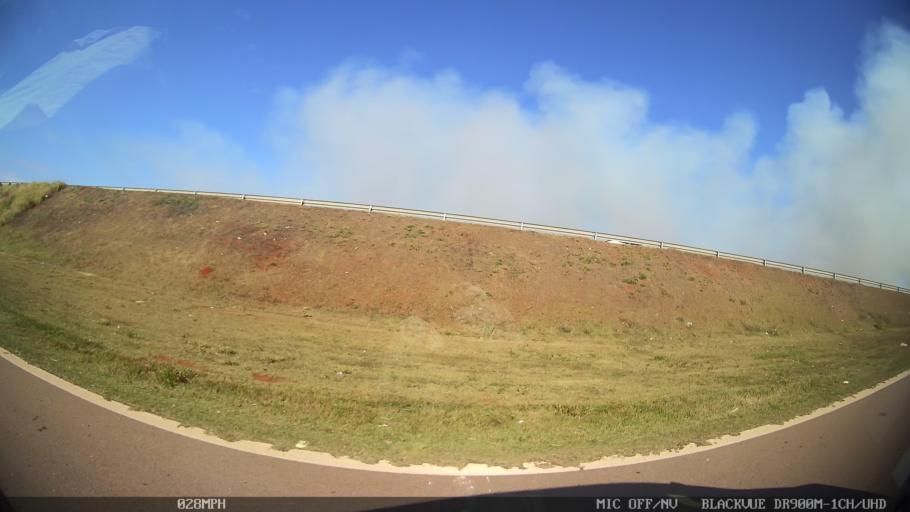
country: BR
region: Sao Paulo
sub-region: Piracicaba
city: Piracicaba
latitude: -22.6925
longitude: -47.6014
